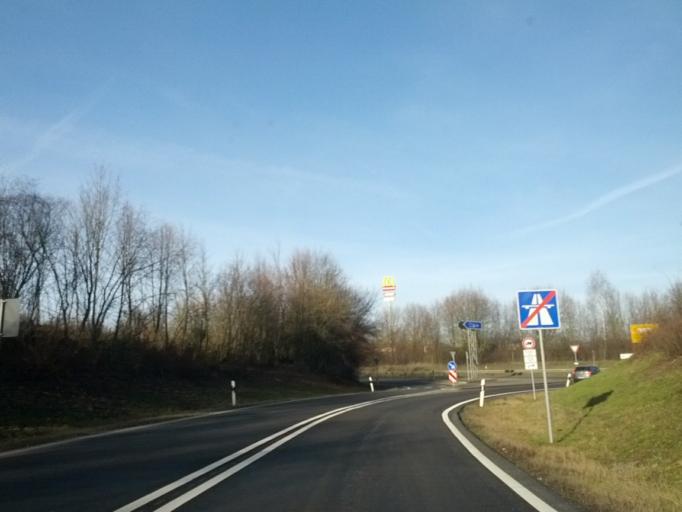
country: DE
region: Baden-Wuerttemberg
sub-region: Regierungsbezirk Stuttgart
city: Ellwangen
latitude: 48.9541
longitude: 10.1849
